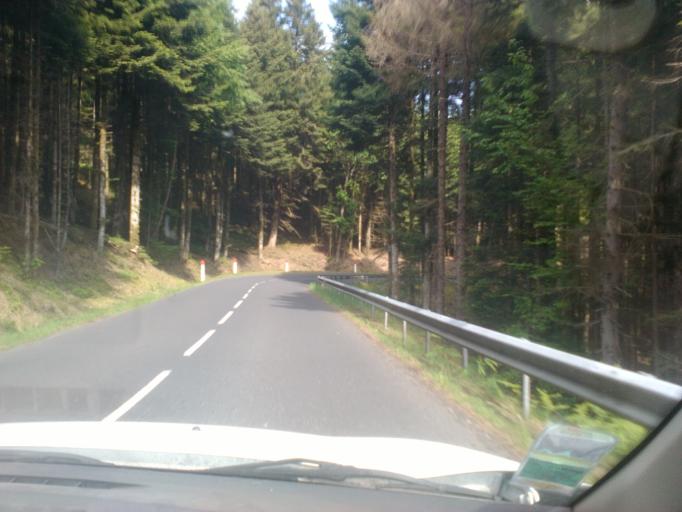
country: FR
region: Lorraine
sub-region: Departement des Vosges
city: Etival-Clairefontaine
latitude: 48.3700
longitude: 6.7943
